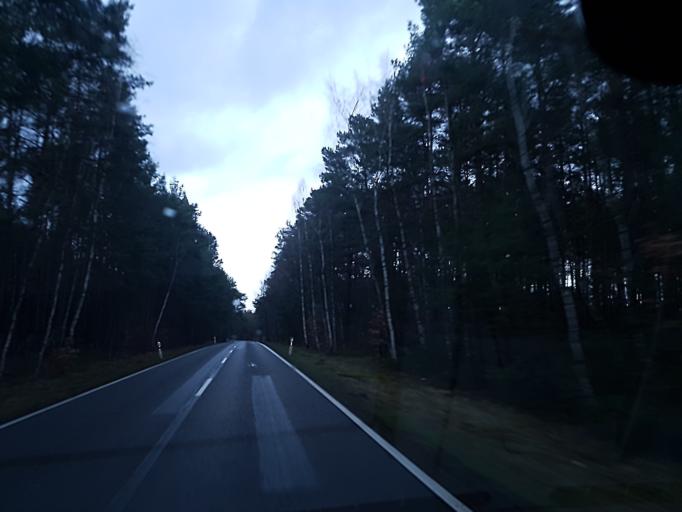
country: DE
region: Brandenburg
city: Finsterwalde
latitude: 51.5465
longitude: 13.6701
